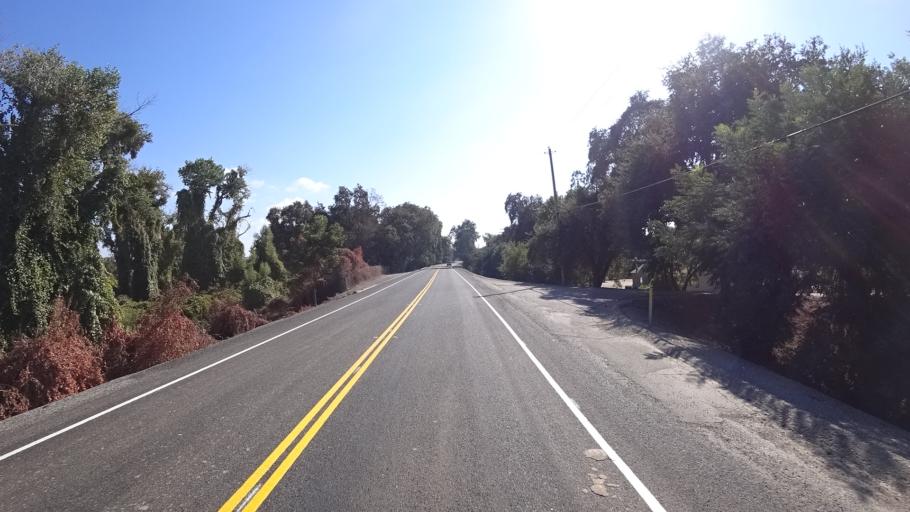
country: US
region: California
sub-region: Yolo County
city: West Sacramento
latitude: 38.6554
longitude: -121.6069
